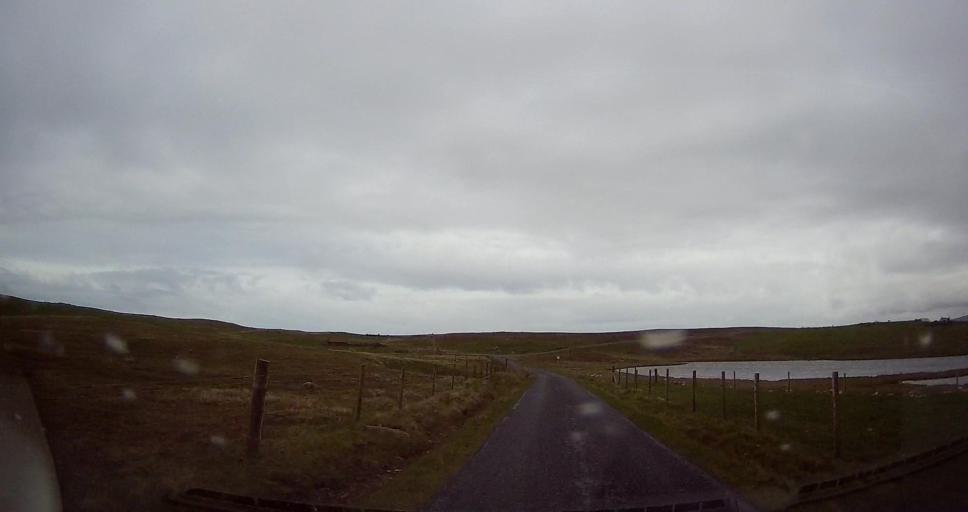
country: GB
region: Scotland
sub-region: Shetland Islands
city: Lerwick
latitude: 60.4828
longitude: -1.6081
